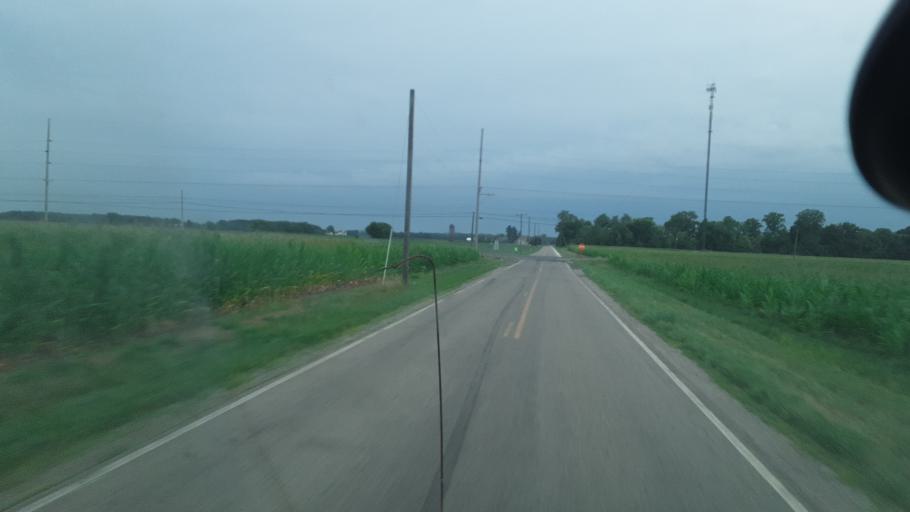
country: US
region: Ohio
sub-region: Defiance County
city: Hicksville
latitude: 41.2670
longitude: -84.7601
